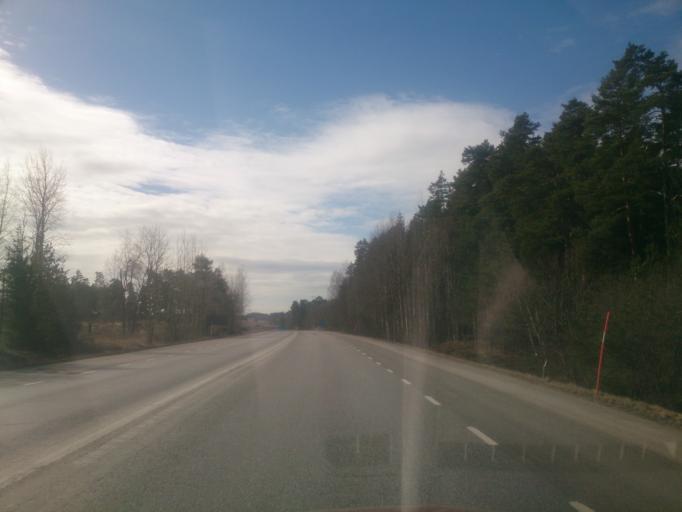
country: SE
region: OEstergoetland
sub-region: Norrkopings Kommun
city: Kimstad
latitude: 58.4936
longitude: 15.9544
